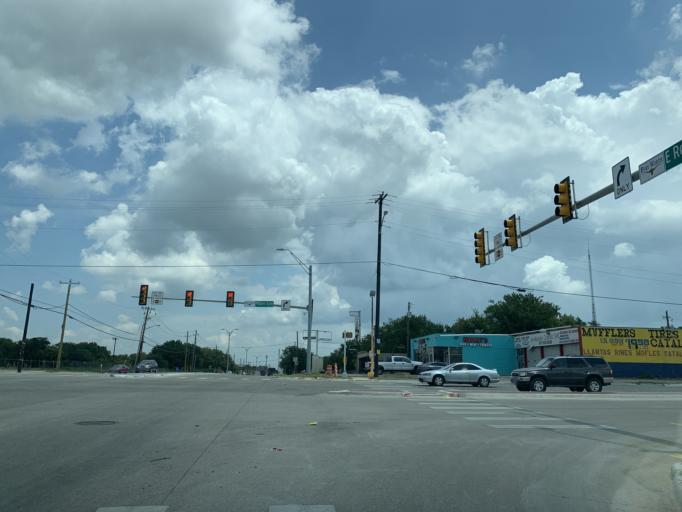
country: US
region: Texas
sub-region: Tarrant County
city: Fort Worth
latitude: 32.7312
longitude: -97.2622
